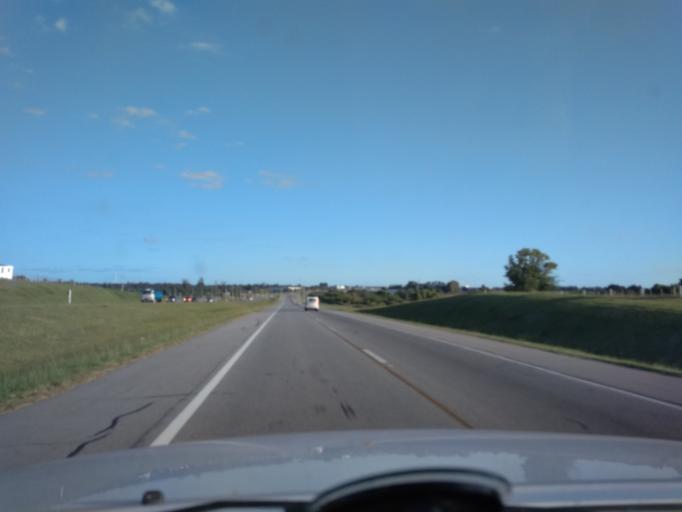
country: UY
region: Canelones
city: Progreso
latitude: -34.6857
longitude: -56.2405
